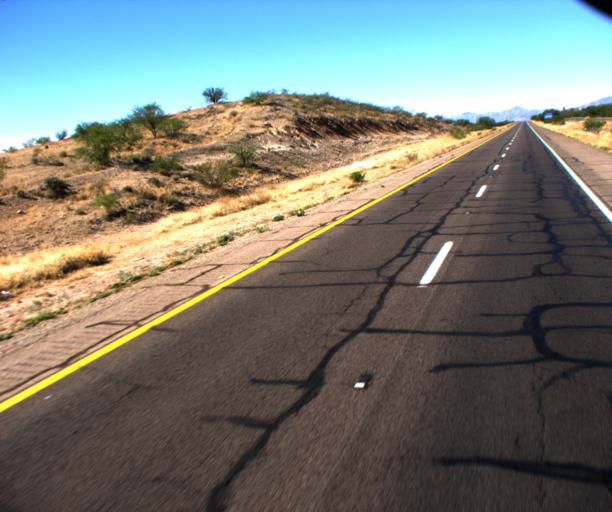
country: US
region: Arizona
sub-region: Pima County
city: Green Valley
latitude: 31.8111
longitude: -111.0107
